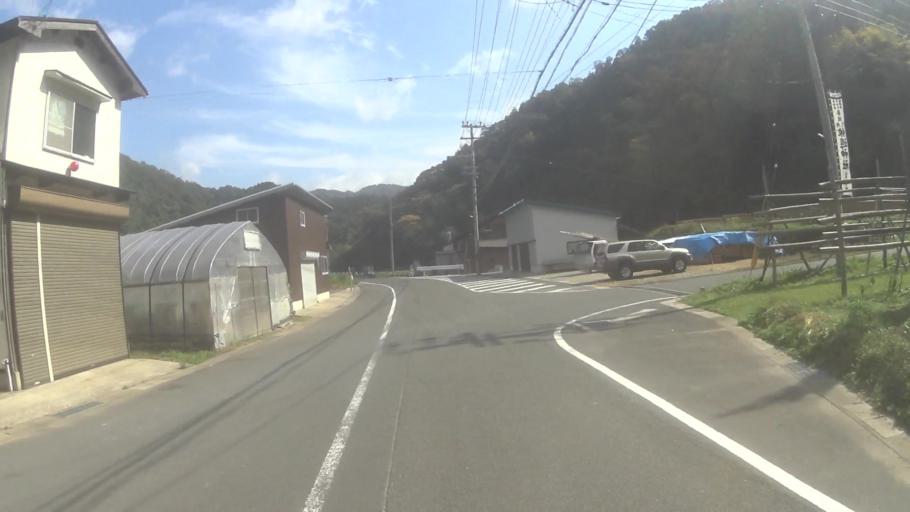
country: JP
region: Kyoto
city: Miyazu
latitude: 35.7354
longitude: 135.1531
